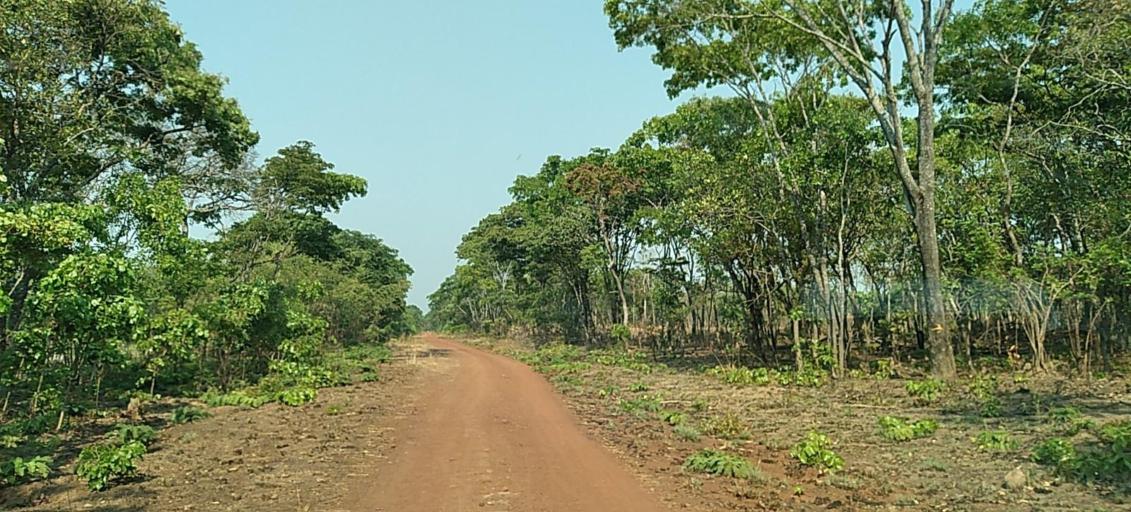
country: ZM
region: Copperbelt
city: Chingola
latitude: -12.8798
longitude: 27.4385
